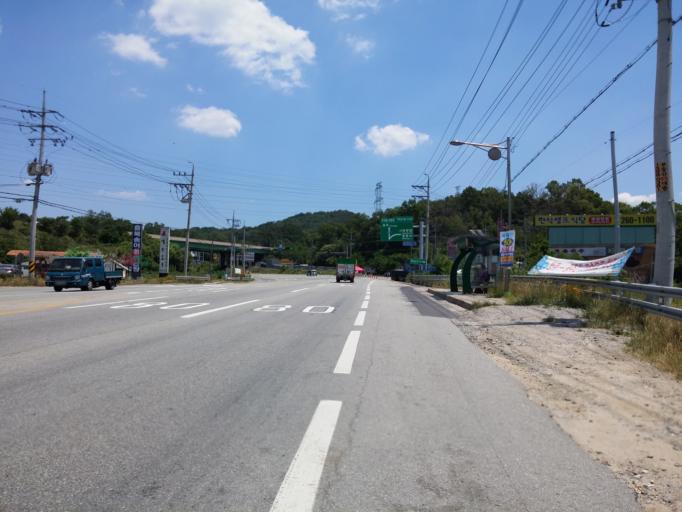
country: KR
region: Chungcheongbuk-do
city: Cheongju-si
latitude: 36.5622
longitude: 127.4460
